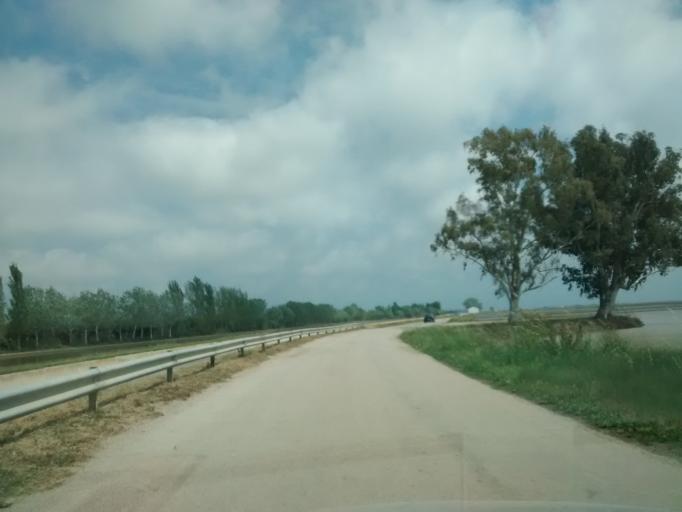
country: ES
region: Catalonia
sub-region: Provincia de Tarragona
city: Deltebre
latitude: 40.6927
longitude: 0.7913
